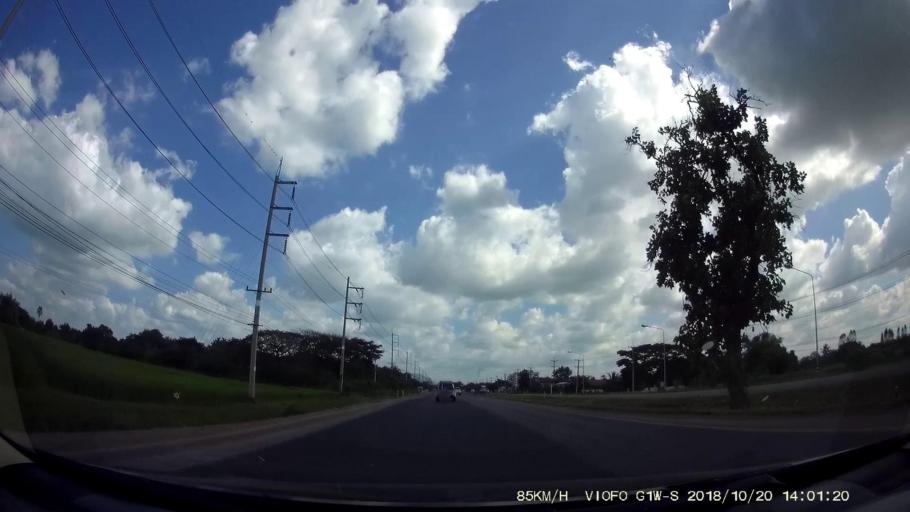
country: TH
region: Khon Kaen
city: Chum Phae
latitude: 16.5030
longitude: 102.1197
